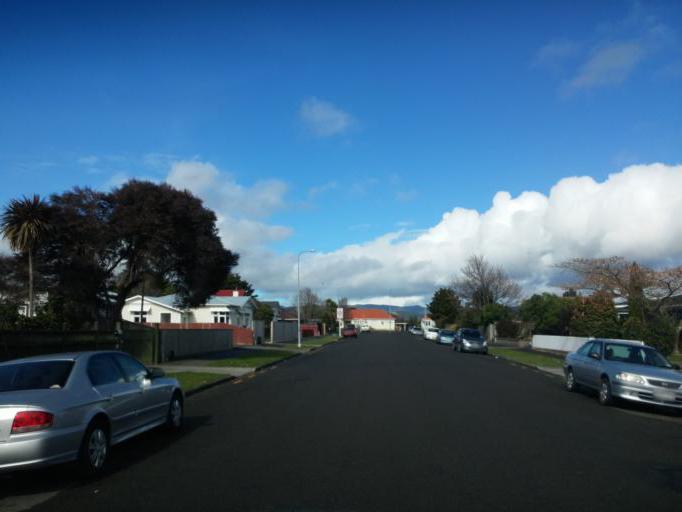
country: NZ
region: Manawatu-Wanganui
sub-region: Palmerston North City
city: Palmerston North
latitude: -40.3589
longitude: 175.6198
